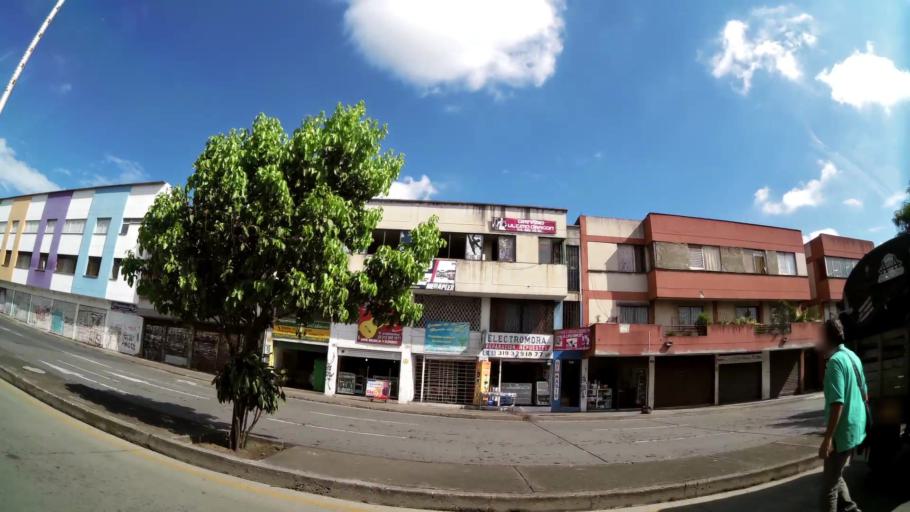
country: CO
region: Valle del Cauca
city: Cali
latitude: 3.4466
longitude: -76.5352
